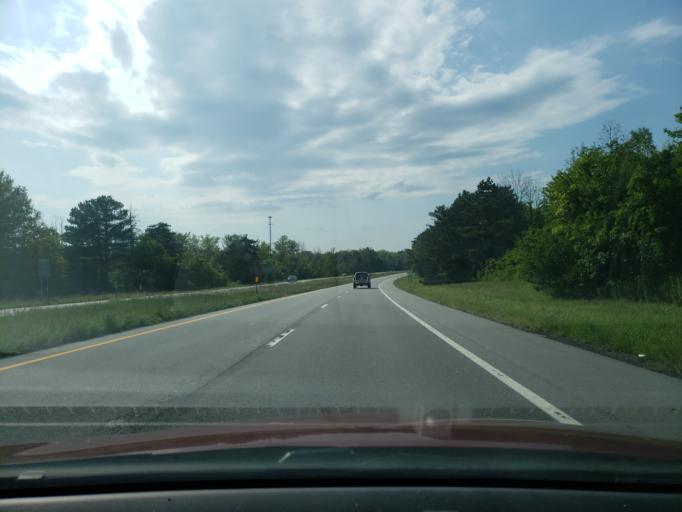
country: US
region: New York
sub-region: Monroe County
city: Greece
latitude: 43.2623
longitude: -77.6495
